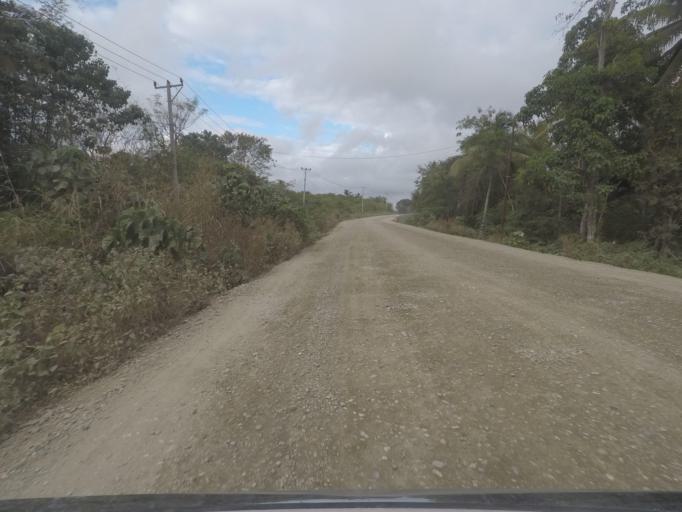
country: TL
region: Baucau
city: Baucau
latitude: -8.4980
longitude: 126.4523
